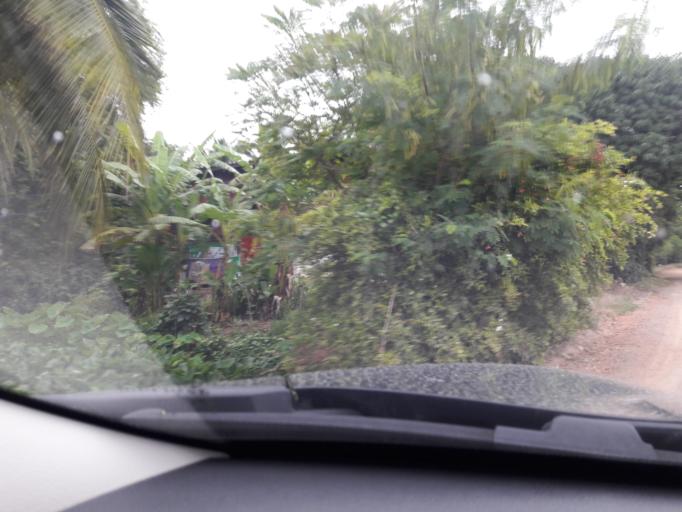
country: TH
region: Ratchaburi
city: Bang Phae
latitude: 13.6240
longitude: 99.9628
